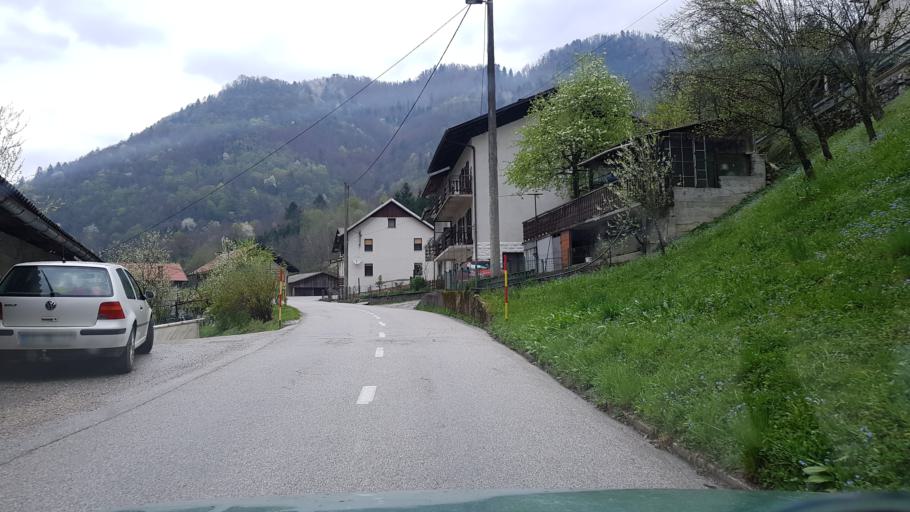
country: SI
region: Tolmin
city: Tolmin
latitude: 46.1208
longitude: 13.8047
